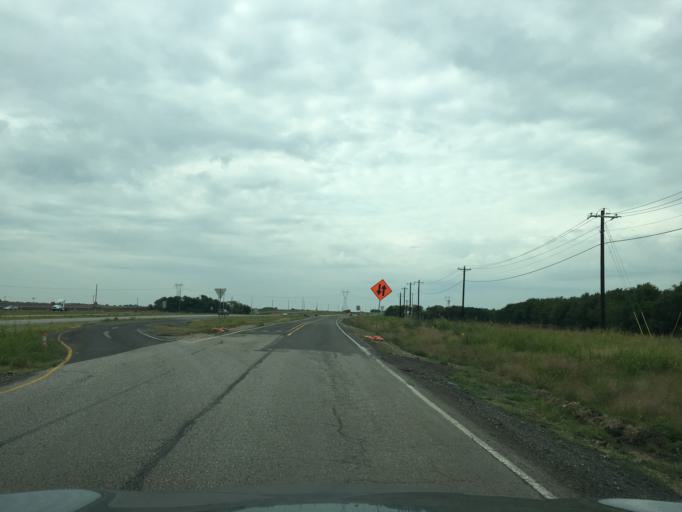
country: US
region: Texas
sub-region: Grayson County
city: Van Alstyne
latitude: 33.3808
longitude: -96.5816
